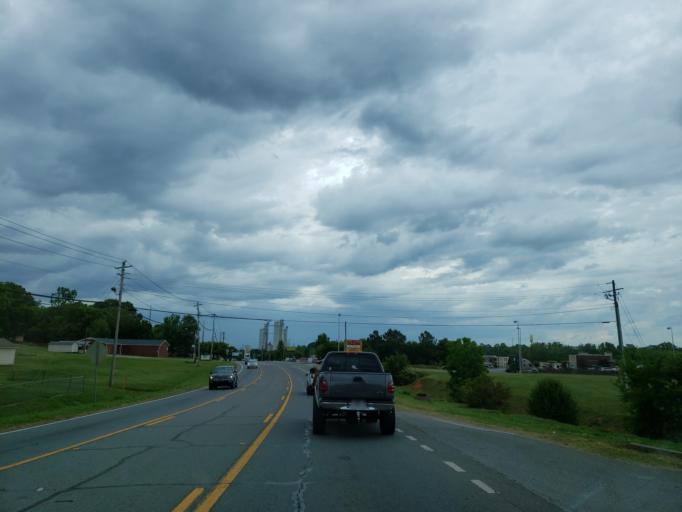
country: US
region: Georgia
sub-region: Polk County
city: Rockmart
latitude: 34.0076
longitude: -85.0420
